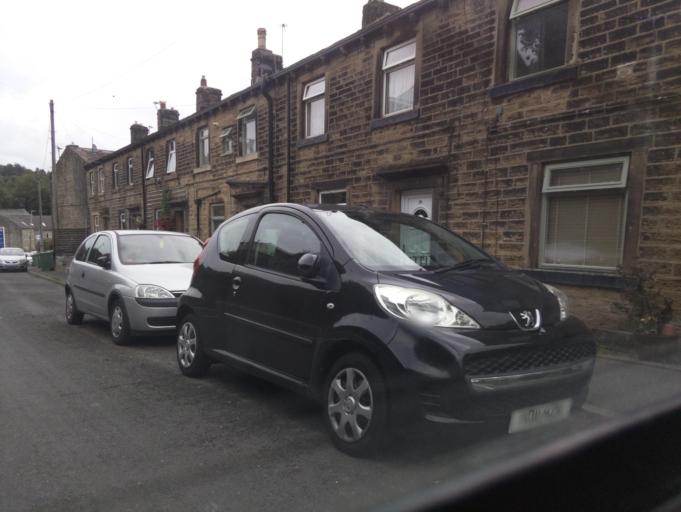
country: GB
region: England
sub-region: Kirklees
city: Holmfirth
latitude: 53.5647
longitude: -1.8039
